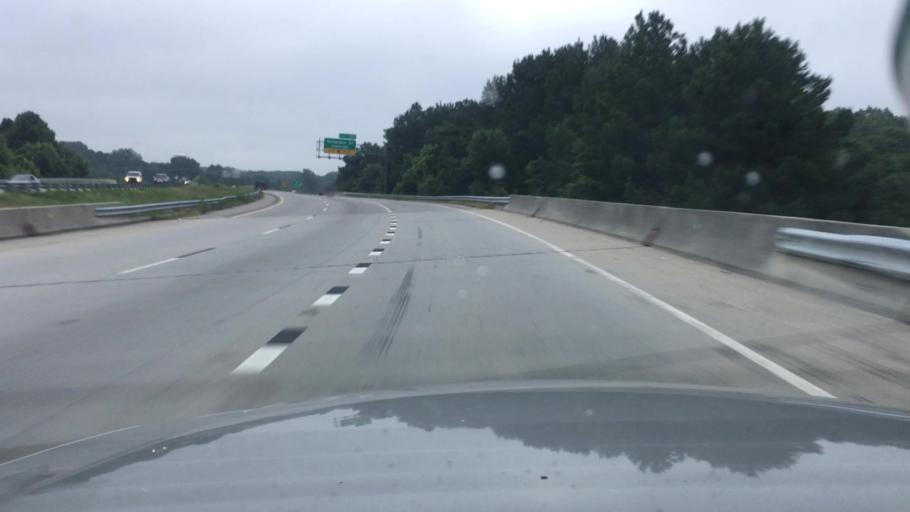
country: US
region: North Carolina
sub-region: Cumberland County
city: Fayetteville
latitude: 35.0387
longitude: -78.8896
